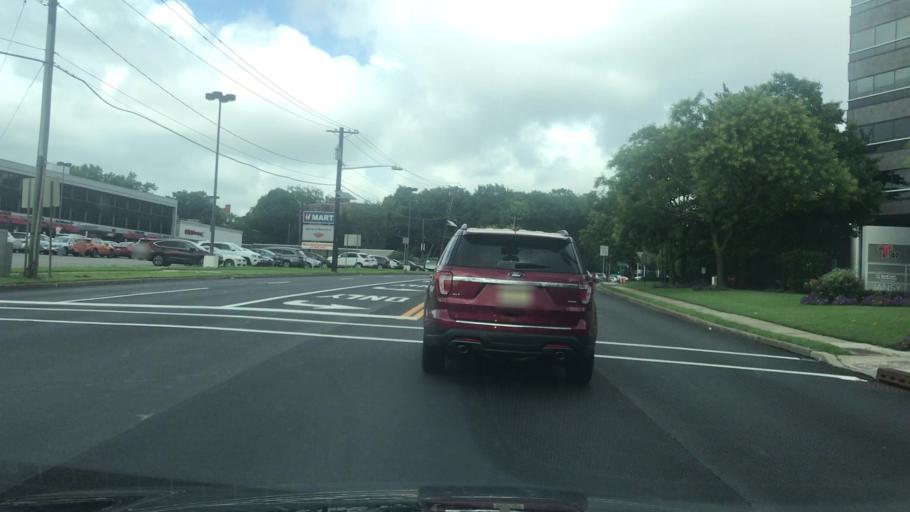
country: US
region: New Jersey
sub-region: Bergen County
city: Fort Lee
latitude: 40.8602
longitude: -73.9708
